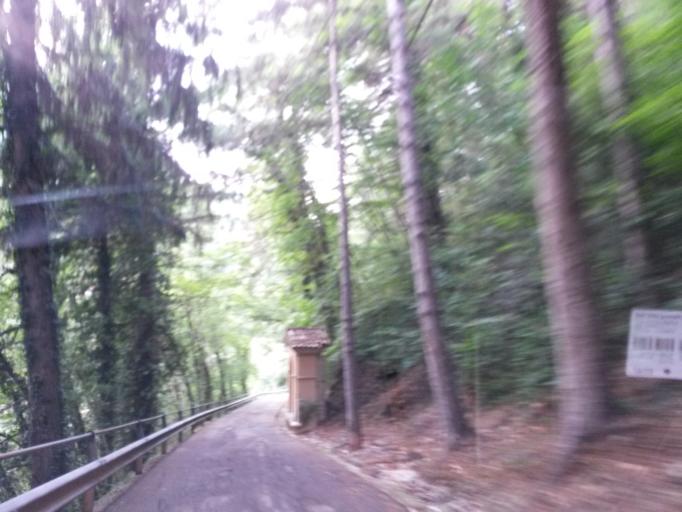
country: IT
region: Lombardy
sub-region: Provincia di Brescia
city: Gardola
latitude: 45.7407
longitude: 10.7315
